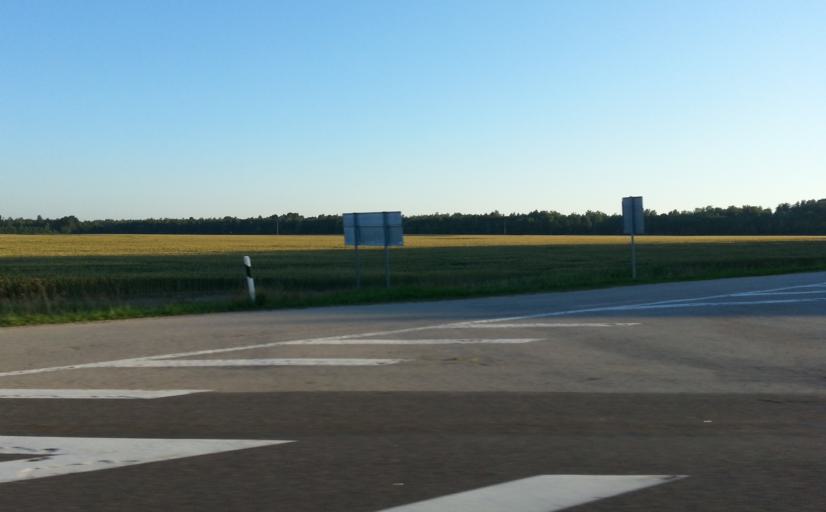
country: LT
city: Ramygala
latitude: 55.5528
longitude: 24.5167
